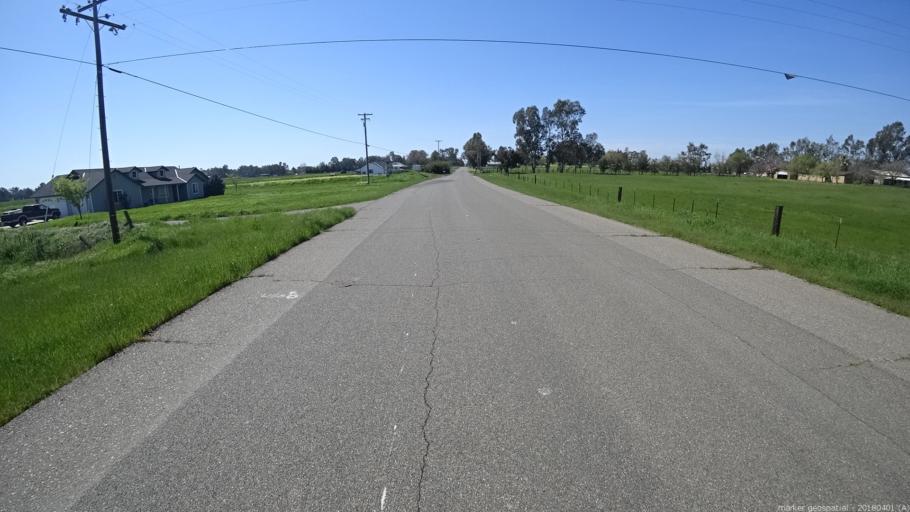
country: US
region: California
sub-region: Sacramento County
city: Wilton
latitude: 38.3941
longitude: -121.2055
